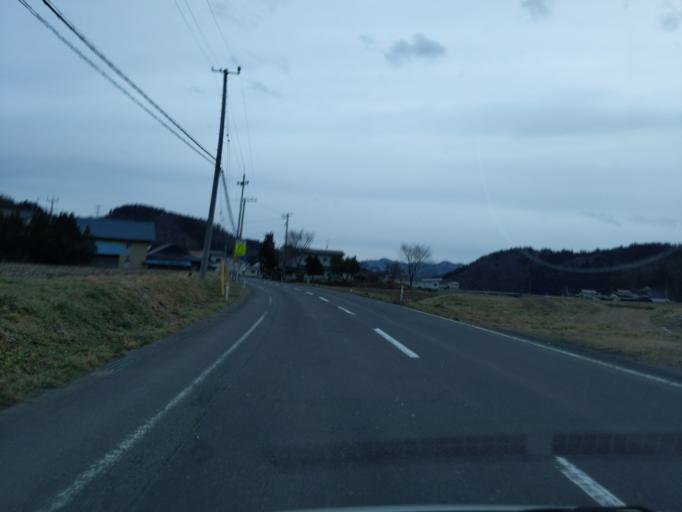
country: JP
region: Iwate
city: Mizusawa
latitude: 39.0426
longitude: 141.2937
